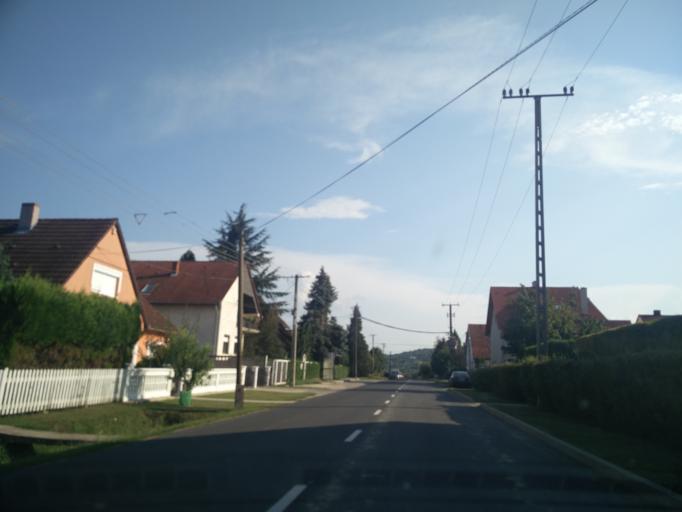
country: HU
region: Zala
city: Zalaegerszeg
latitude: 46.8664
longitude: 16.8072
